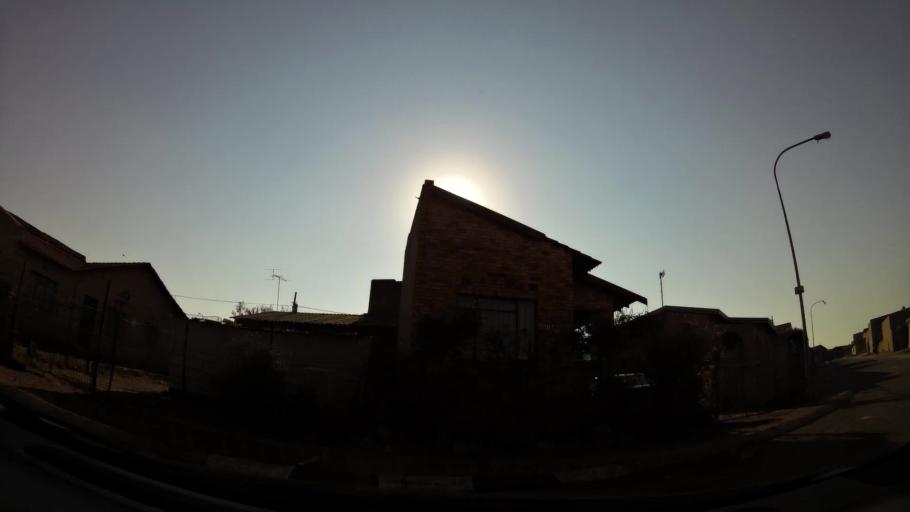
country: ZA
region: Gauteng
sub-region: City of Johannesburg Metropolitan Municipality
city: Soweto
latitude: -26.2538
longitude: 27.9475
